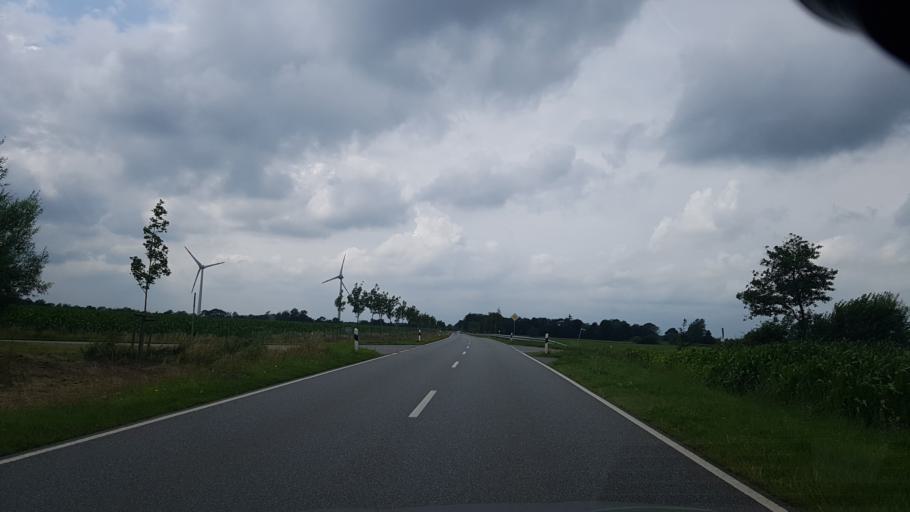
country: DE
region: Schleswig-Holstein
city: Weesby
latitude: 54.8590
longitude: 9.1545
